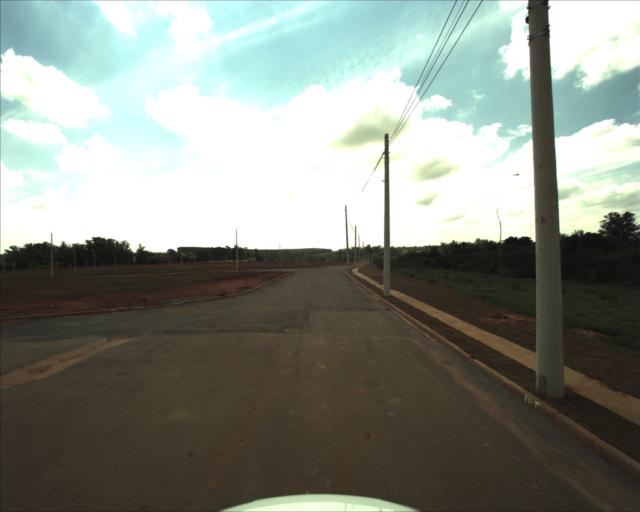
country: BR
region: Sao Paulo
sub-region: Sorocaba
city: Sorocaba
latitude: -23.4047
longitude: -47.4069
